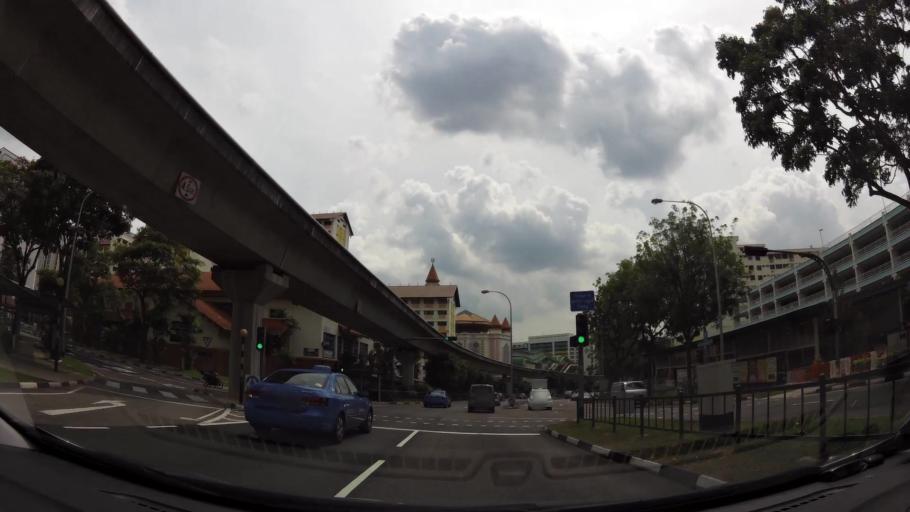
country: MY
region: Johor
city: Johor Bahru
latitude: 1.3796
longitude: 103.7725
